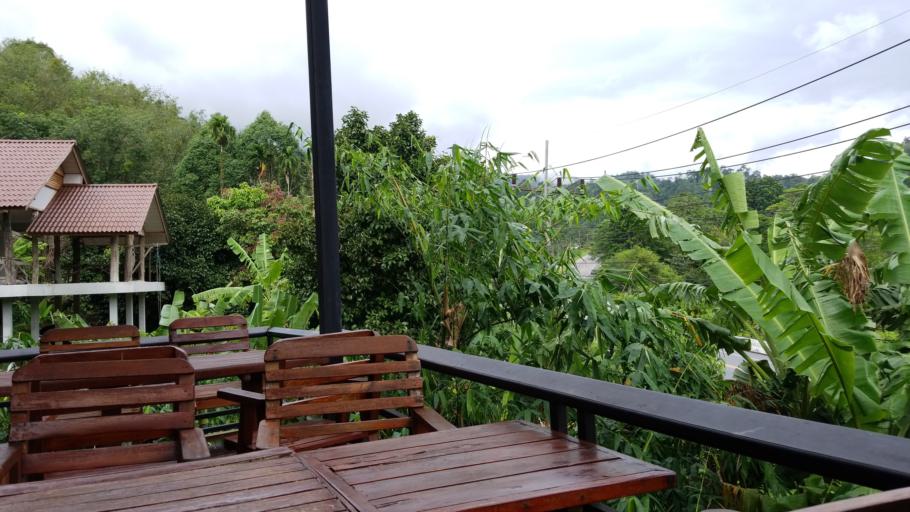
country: TH
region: Nakhon Si Thammarat
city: Lan Saka
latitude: 8.3482
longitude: 99.7258
